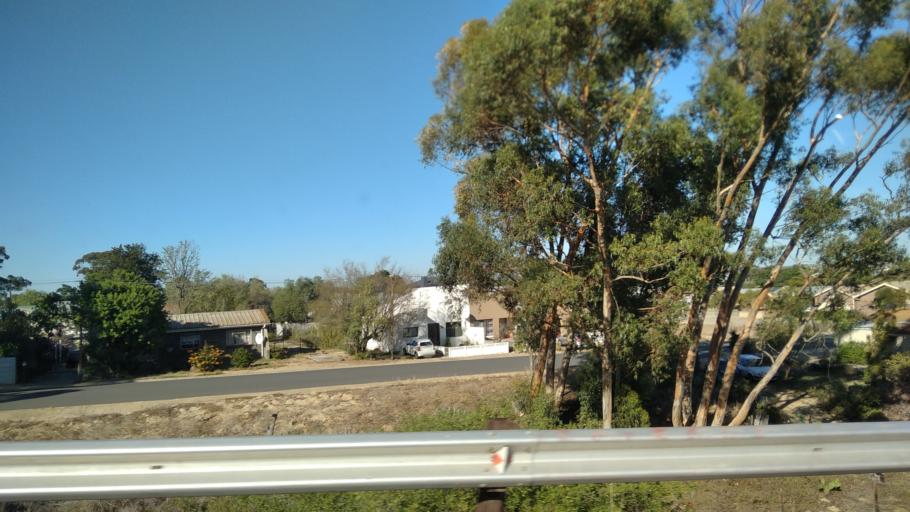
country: ZA
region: Western Cape
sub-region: West Coast District Municipality
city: Moorreesburg
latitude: -33.0602
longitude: 18.3529
